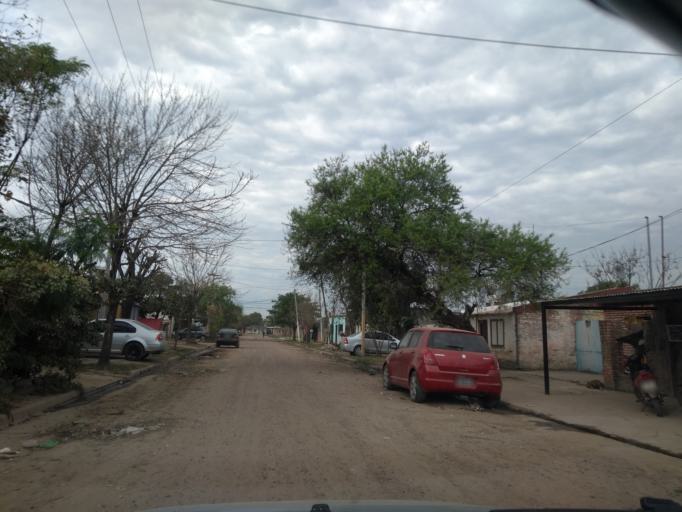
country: AR
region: Chaco
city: Resistencia
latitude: -27.4795
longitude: -58.9800
